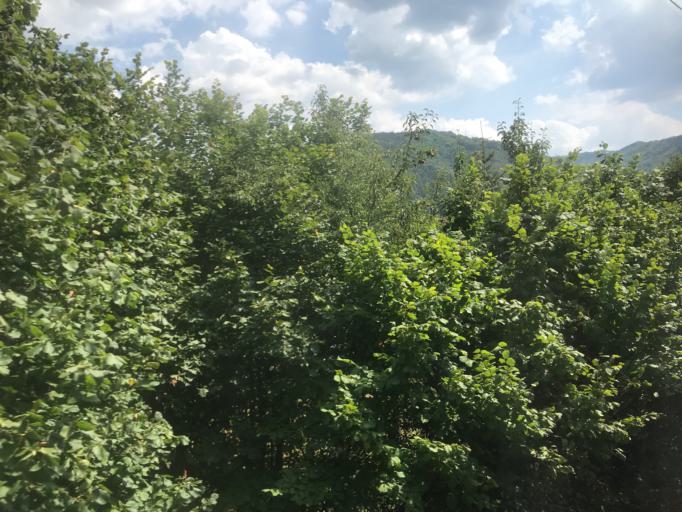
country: CZ
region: Ustecky
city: Povrly
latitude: 50.6970
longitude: 14.1982
